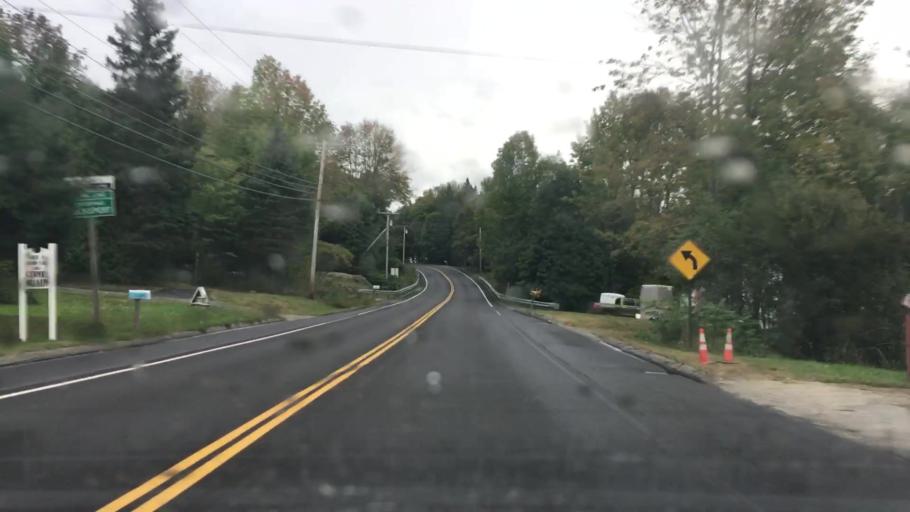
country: US
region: Maine
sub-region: Penobscot County
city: Orrington
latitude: 44.6852
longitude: -68.8107
